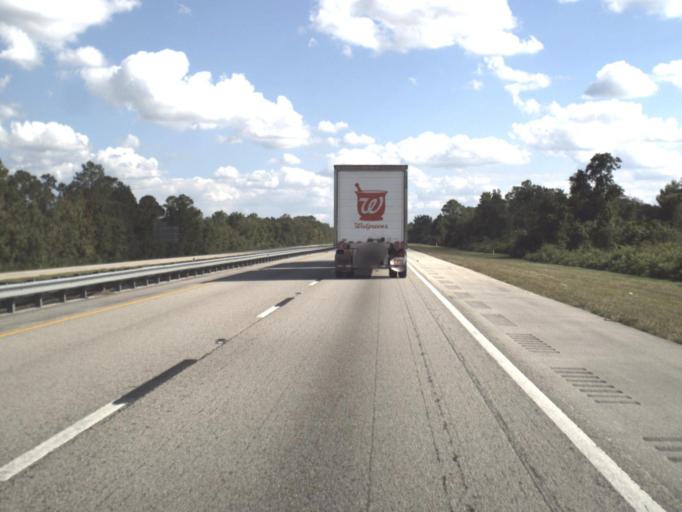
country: US
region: Florida
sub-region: Indian River County
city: Fellsmere
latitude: 27.6749
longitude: -80.8853
